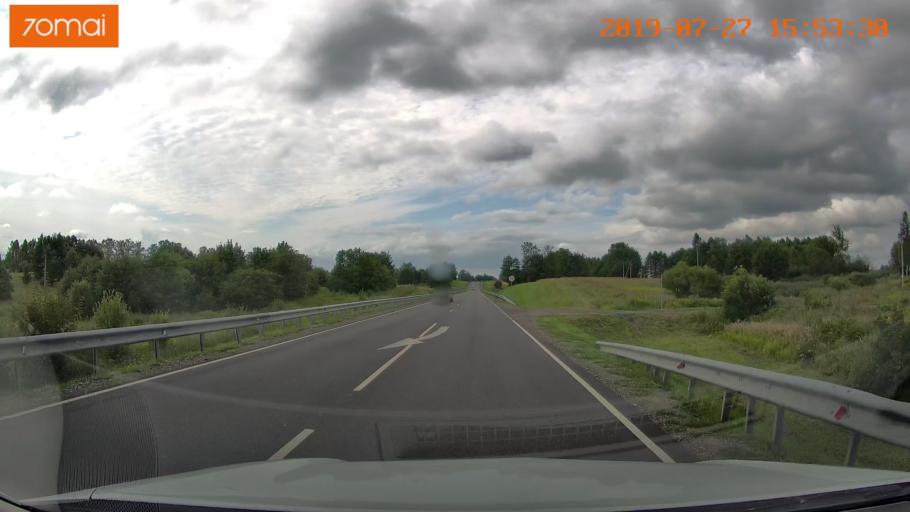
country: RU
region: Kaliningrad
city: Chernyakhovsk
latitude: 54.6037
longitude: 21.9532
